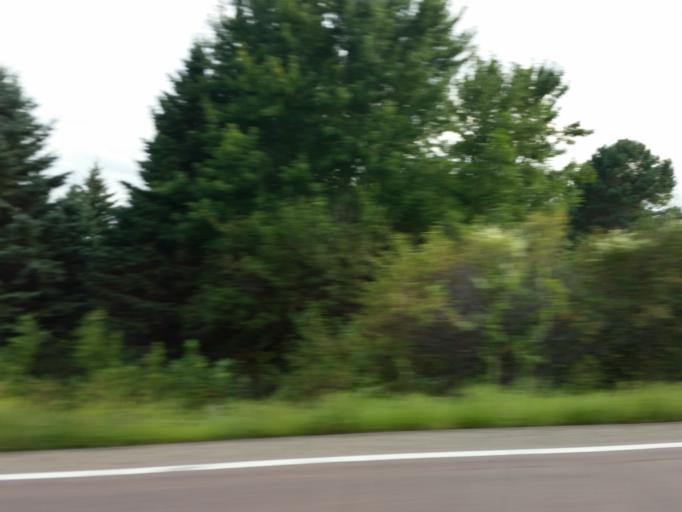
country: US
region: Minnesota
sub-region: Dakota County
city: Farmington
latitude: 44.6304
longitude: -93.0619
